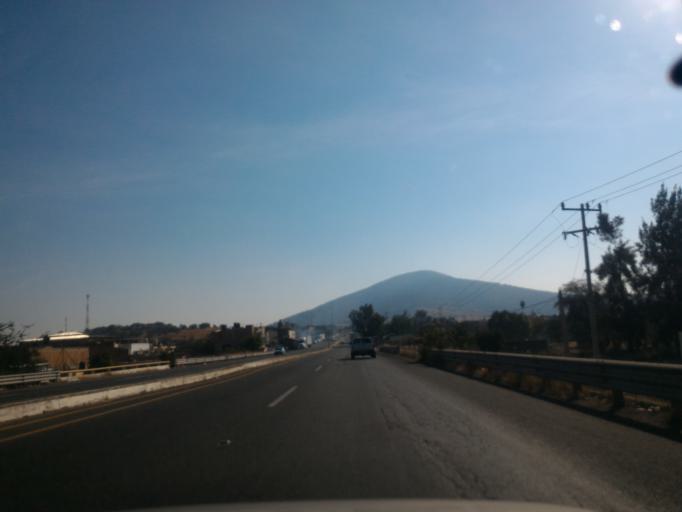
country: MX
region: Jalisco
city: Atotonilquillo
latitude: 20.3912
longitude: -103.1233
